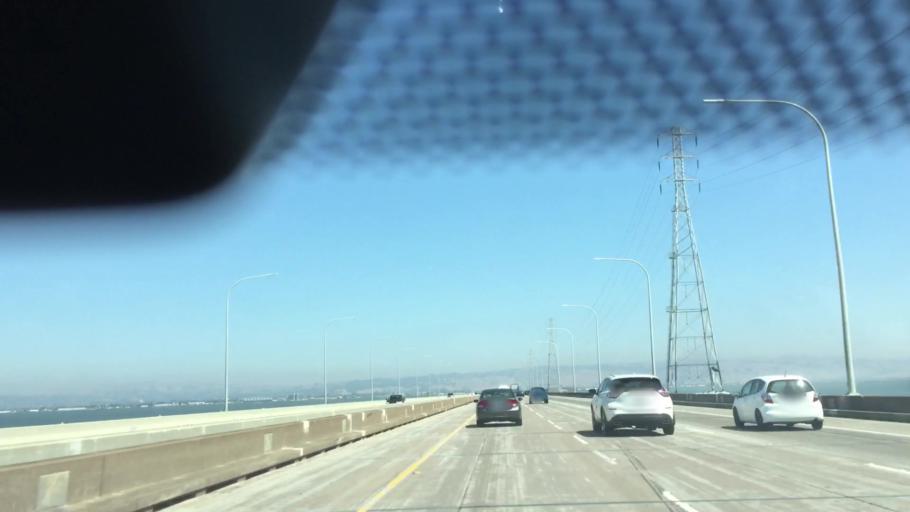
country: US
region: California
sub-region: Alameda County
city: San Lorenzo
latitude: 37.6099
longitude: -122.1826
